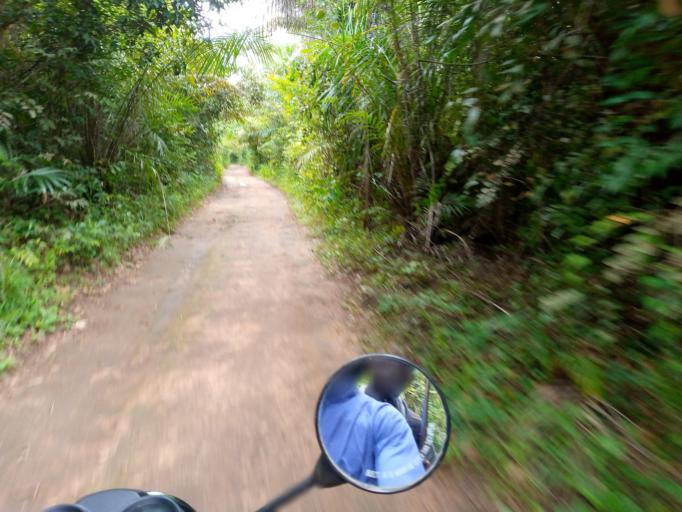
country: SL
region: Northern Province
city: Mange
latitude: 8.9791
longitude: -12.8199
